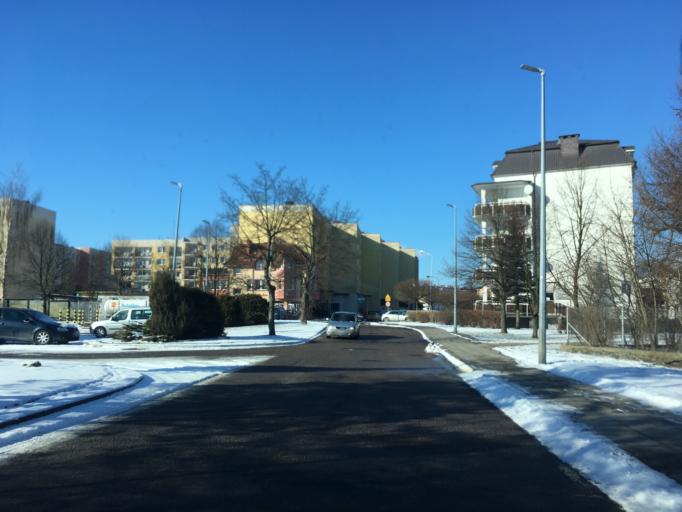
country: PL
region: Pomeranian Voivodeship
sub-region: Powiat slupski
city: Kobylnica
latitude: 54.4593
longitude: 16.9961
